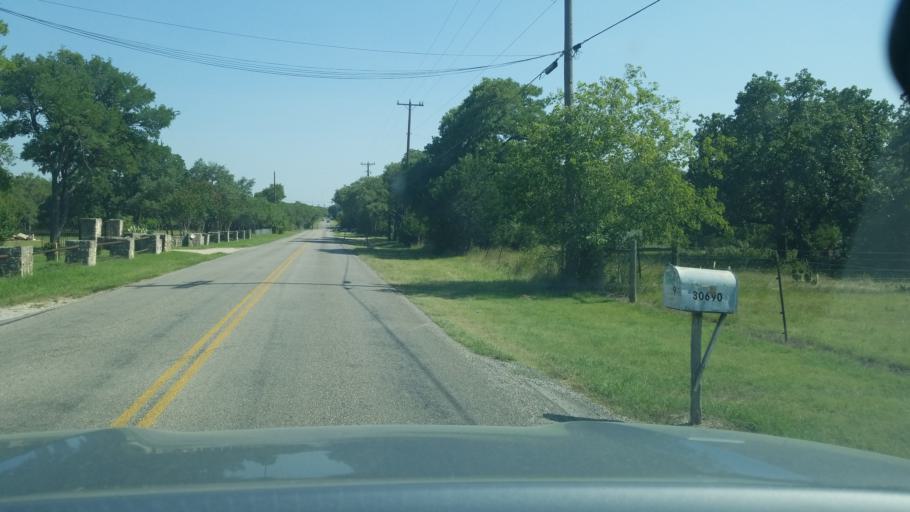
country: US
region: Texas
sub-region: Bexar County
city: Timberwood Park
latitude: 29.7510
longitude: -98.5128
